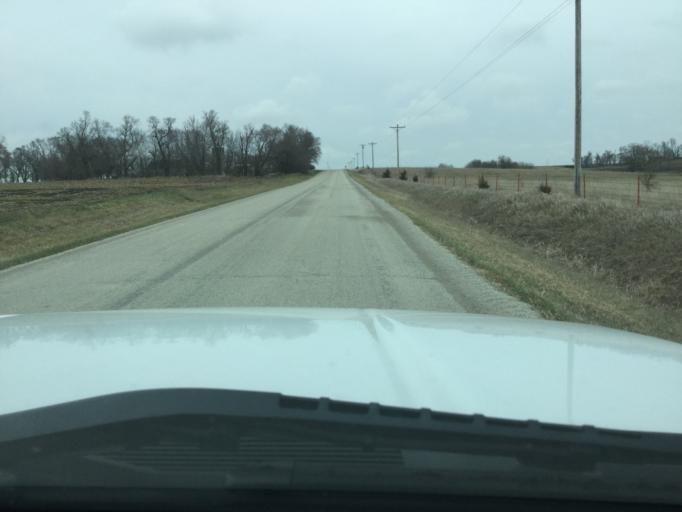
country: US
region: Kansas
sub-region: Nemaha County
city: Sabetha
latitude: 39.8766
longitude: -95.7141
